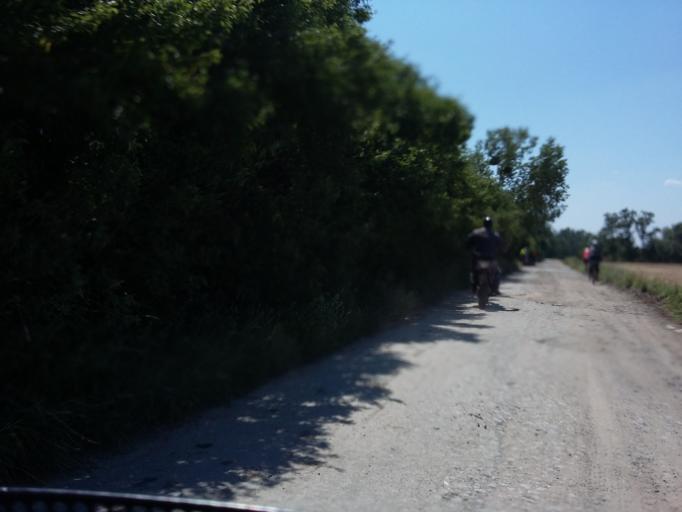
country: AT
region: Lower Austria
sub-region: Politischer Bezirk Ganserndorf
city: Marchegg
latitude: 48.2831
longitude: 16.9676
